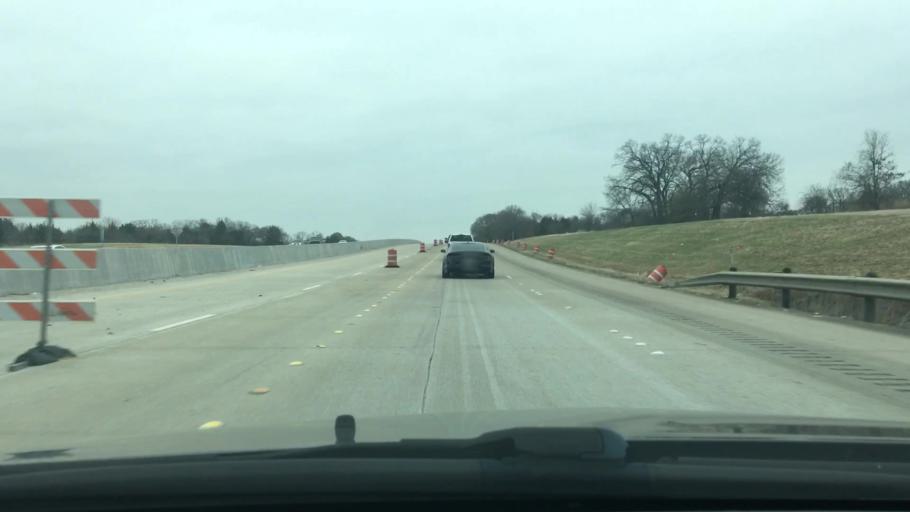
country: US
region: Texas
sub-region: Navarro County
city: Corsicana
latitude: 32.1326
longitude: -96.4555
